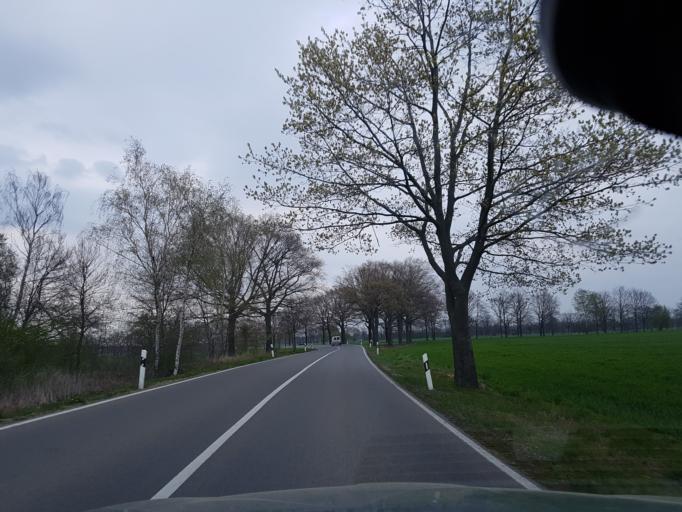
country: DE
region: Brandenburg
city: Schraden
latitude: 51.4206
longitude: 13.7035
